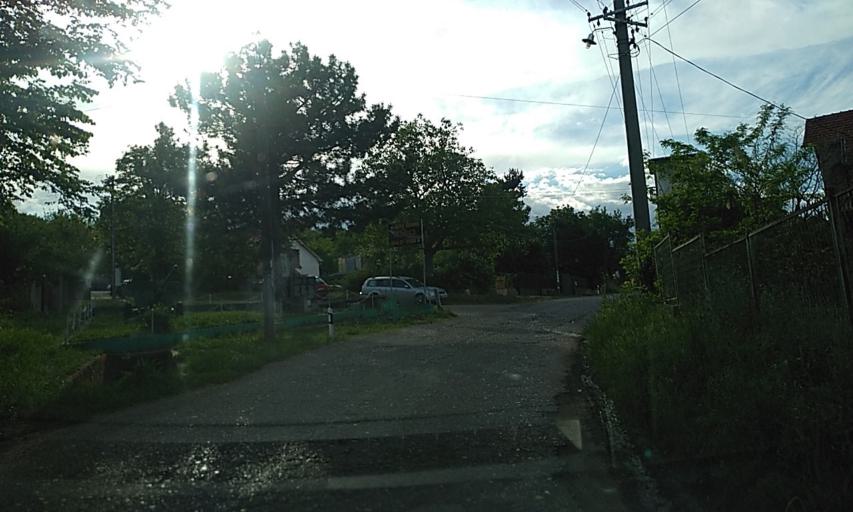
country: RS
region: Central Serbia
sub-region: Nisavski Okrug
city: Merosina
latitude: 43.4109
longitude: 21.7530
